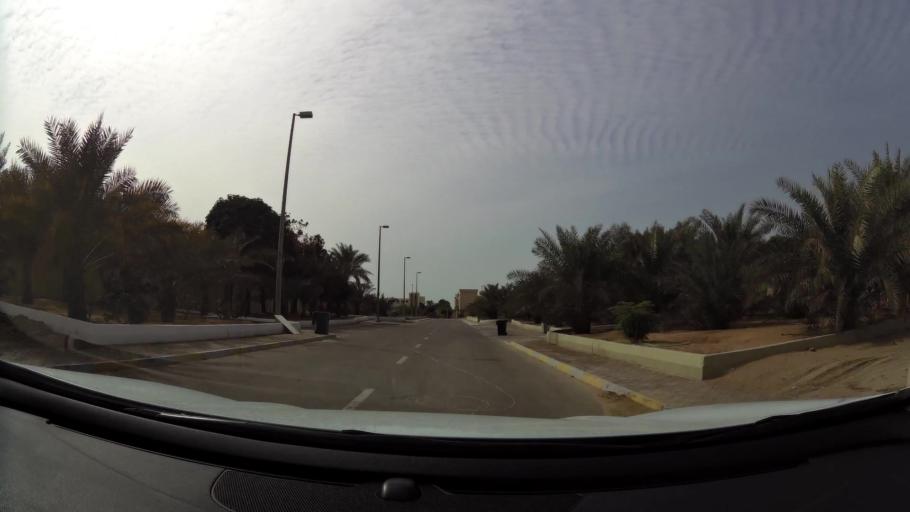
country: AE
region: Abu Dhabi
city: Abu Dhabi
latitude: 24.5729
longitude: 54.6879
